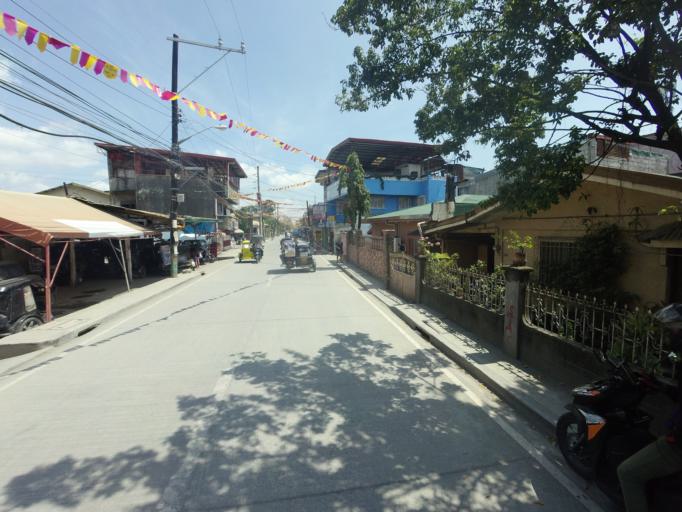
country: PH
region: Calabarzon
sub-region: Province of Rizal
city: Taytay
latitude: 14.5431
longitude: 121.1078
